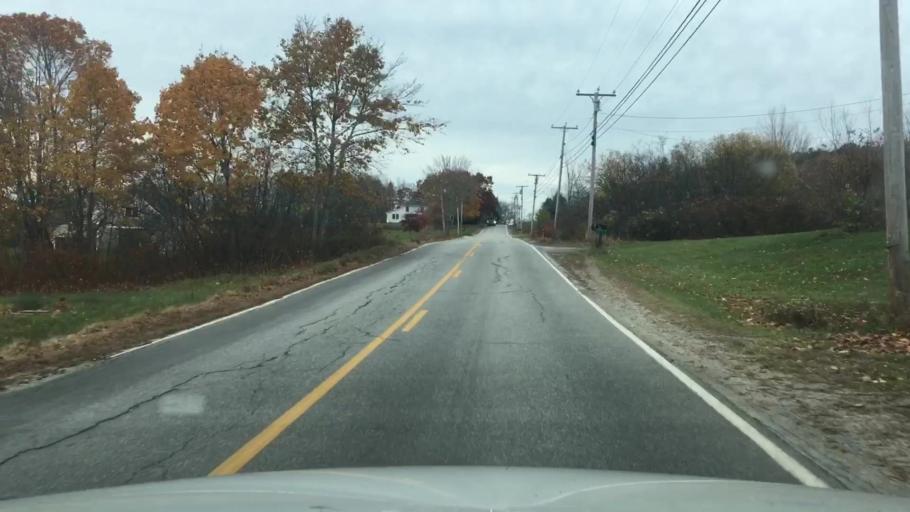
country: US
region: Maine
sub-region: Hancock County
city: Sedgwick
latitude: 44.3537
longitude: -68.5496
